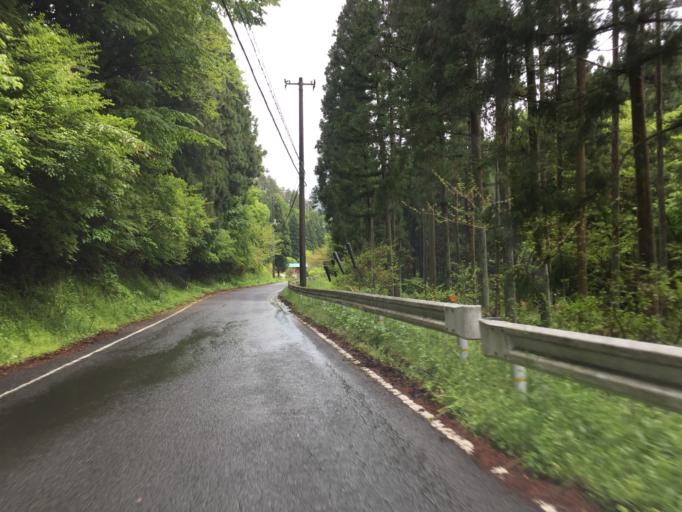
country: JP
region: Fukushima
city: Ishikawa
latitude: 37.0264
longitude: 140.5552
